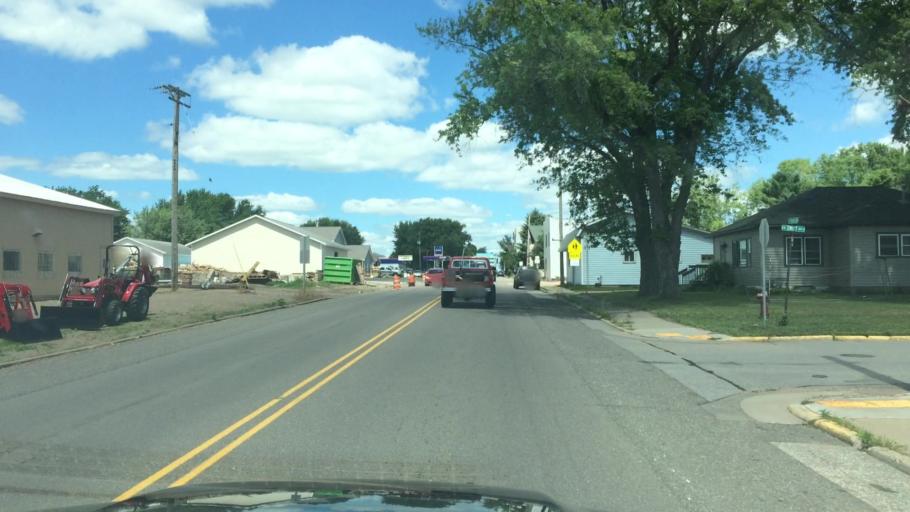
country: US
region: Wisconsin
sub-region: Taylor County
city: Medford
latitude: 45.0745
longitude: -90.3148
